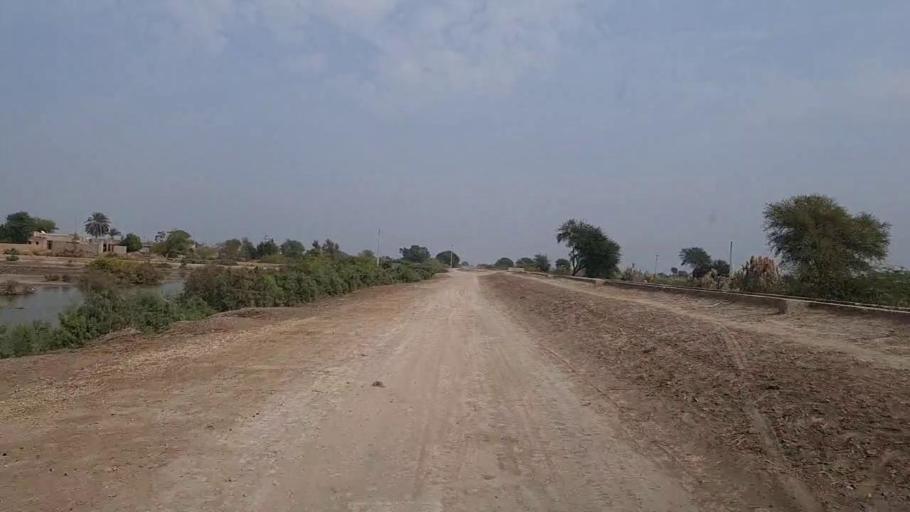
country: PK
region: Sindh
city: Mirwah Gorchani
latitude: 25.3978
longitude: 69.0929
